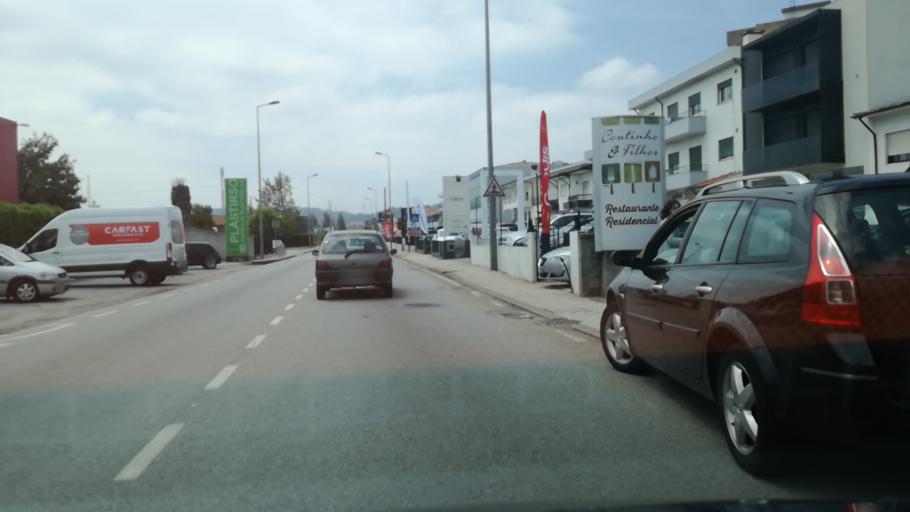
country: PT
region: Porto
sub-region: Trofa
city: Bougado
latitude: 41.3308
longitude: -8.5646
